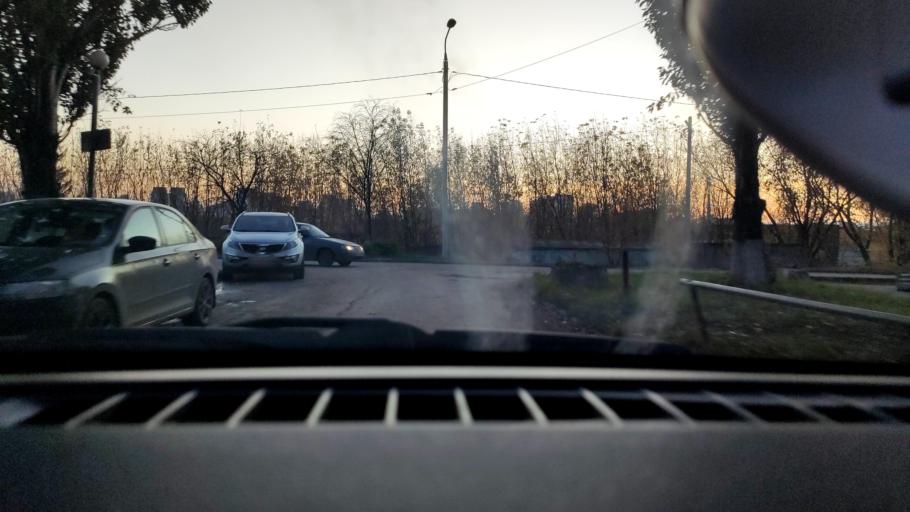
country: RU
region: Perm
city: Perm
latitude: 58.0139
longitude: 56.2787
